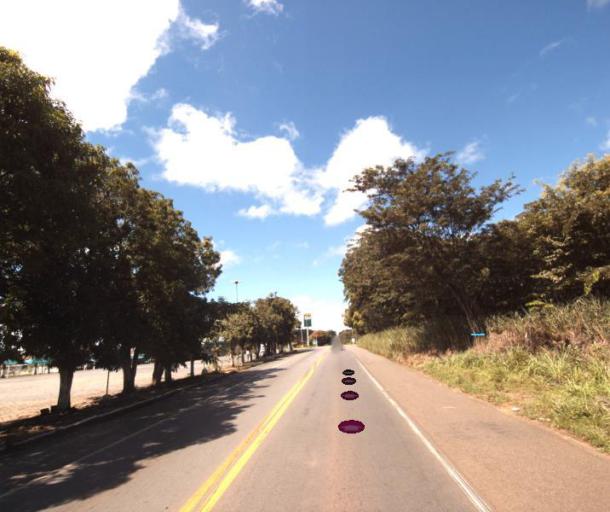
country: BR
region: Goias
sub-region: Jaragua
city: Jaragua
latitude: -15.7849
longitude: -49.3035
